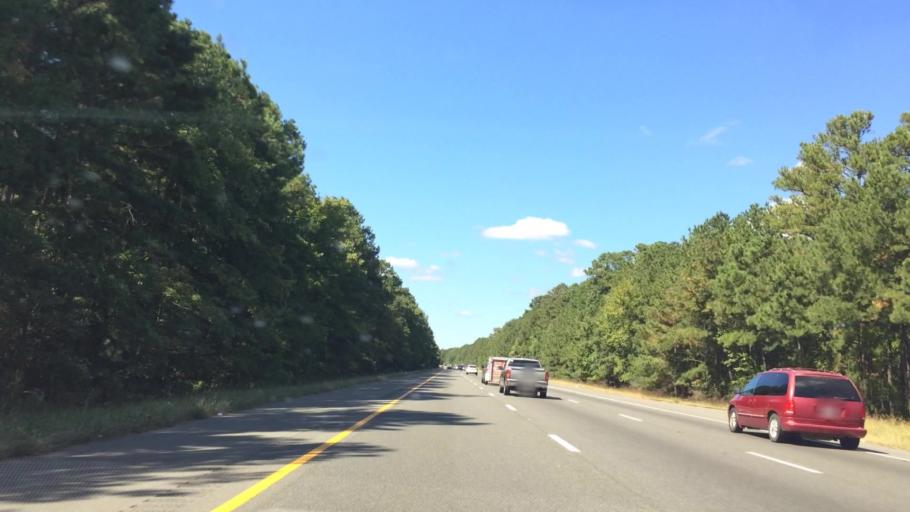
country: US
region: Virginia
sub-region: Henrico County
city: Glen Allen
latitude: 37.6691
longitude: -77.4873
